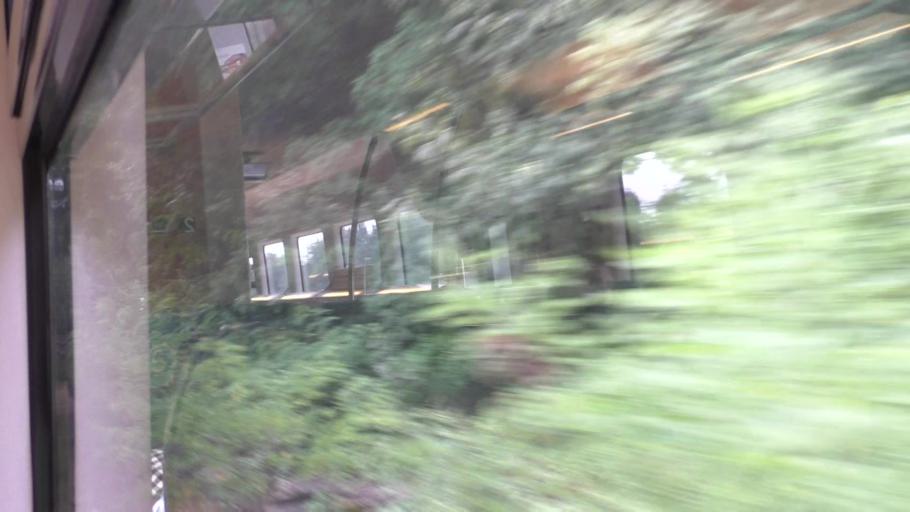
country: DE
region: Saxony
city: Goerlitz
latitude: 51.1605
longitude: 14.9601
